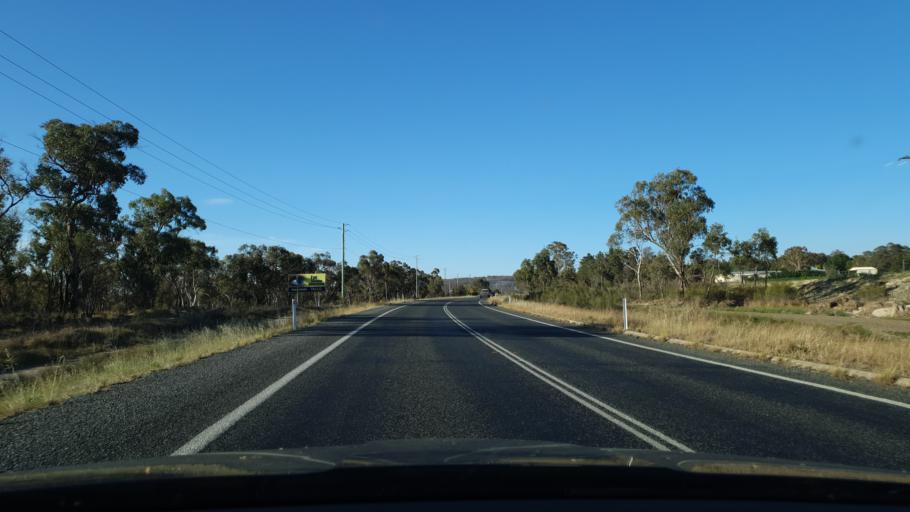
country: AU
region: Queensland
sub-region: Southern Downs
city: Stanthorpe
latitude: -28.6661
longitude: 151.9154
